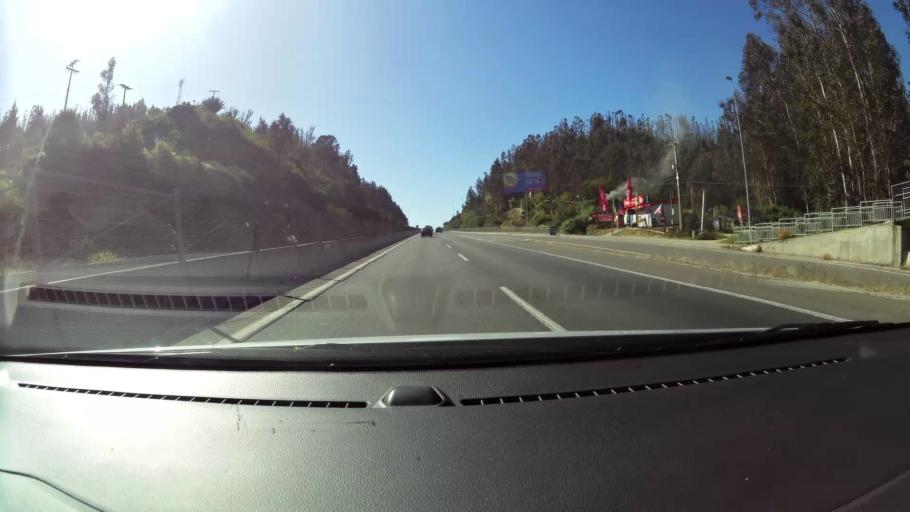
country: CL
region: Valparaiso
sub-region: Provincia de Marga Marga
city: Quilpue
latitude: -33.2085
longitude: -71.4809
